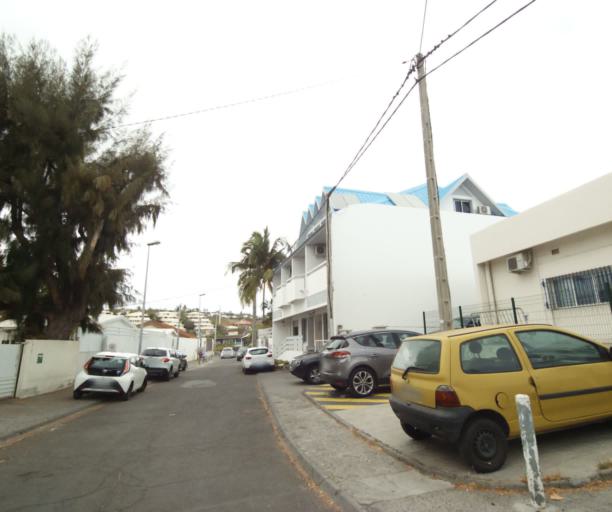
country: RE
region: Reunion
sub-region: Reunion
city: Saint-Paul
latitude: -21.0529
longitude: 55.2247
